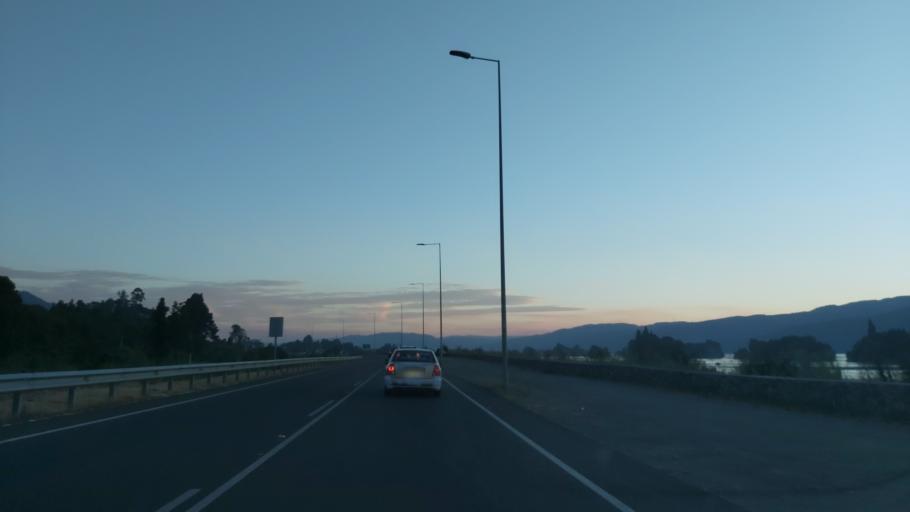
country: CL
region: Biobio
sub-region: Provincia de Concepcion
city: Chiguayante
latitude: -36.8862
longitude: -73.0383
